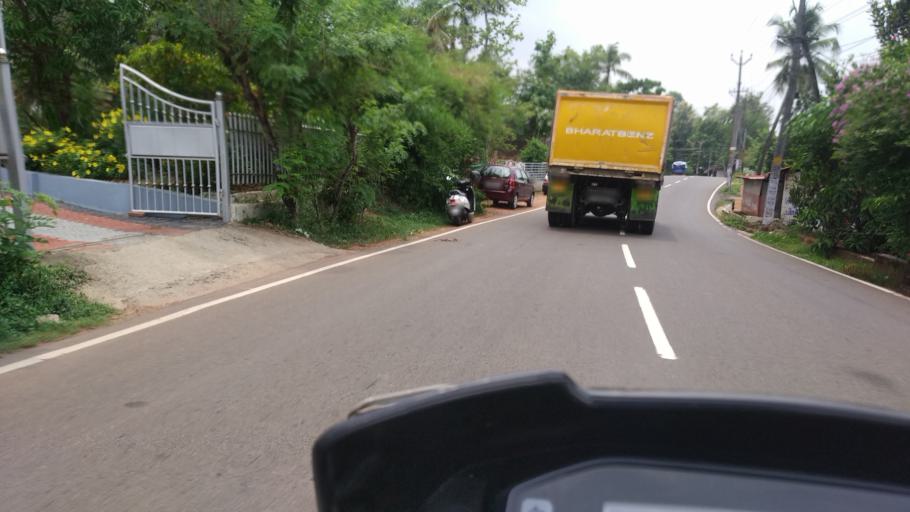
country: IN
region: Kerala
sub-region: Ernakulam
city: Aluva
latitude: 10.1560
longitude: 76.2997
